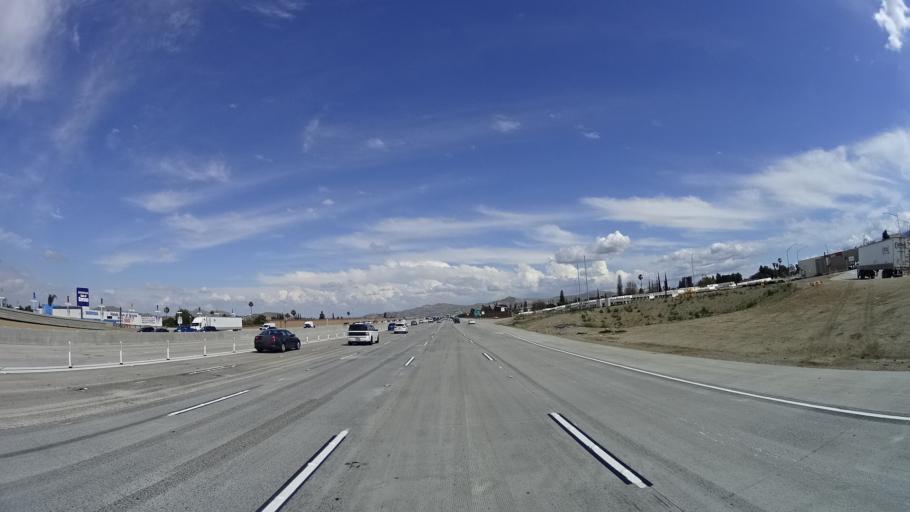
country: US
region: California
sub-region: Riverside County
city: Corona
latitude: 33.8811
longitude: -117.5817
